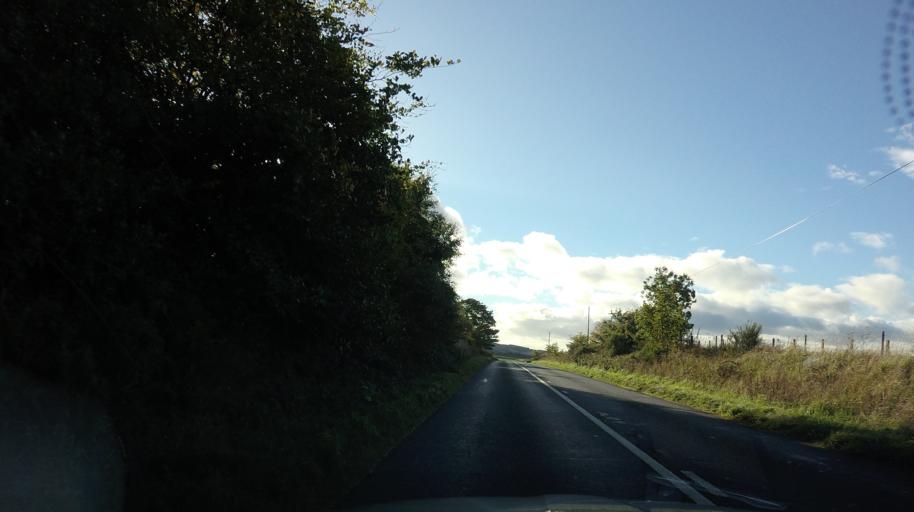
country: GB
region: Scotland
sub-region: Fife
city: Kelty
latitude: 56.1714
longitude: -3.3782
